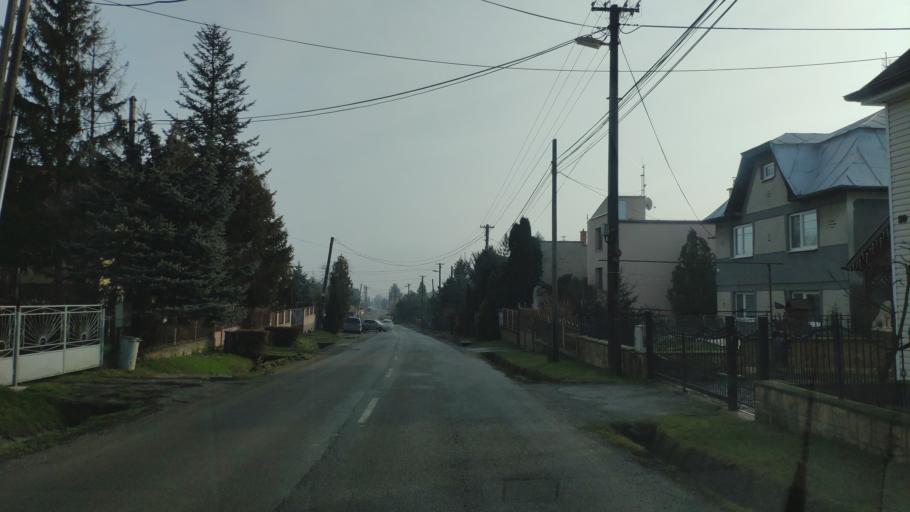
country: SK
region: Kosicky
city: Kosice
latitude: 48.7067
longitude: 21.4052
